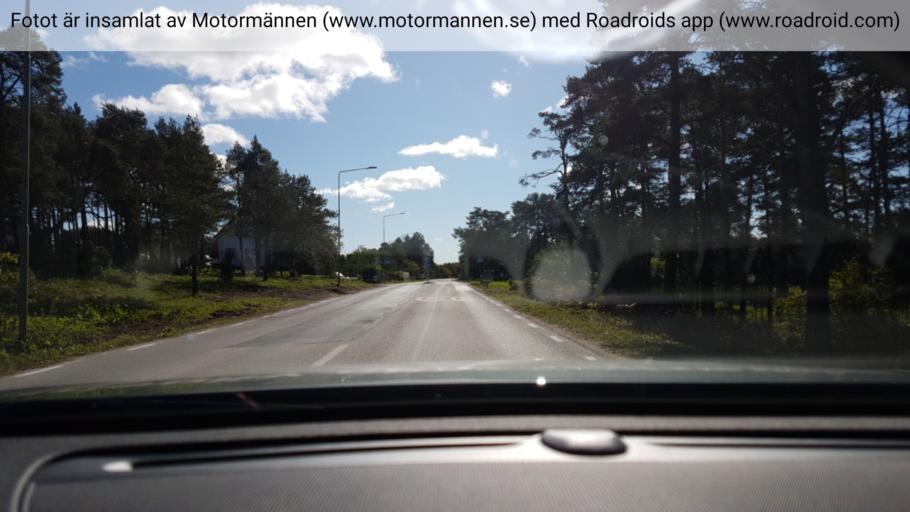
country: SE
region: Gotland
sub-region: Gotland
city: Slite
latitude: 57.7072
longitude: 18.7944
